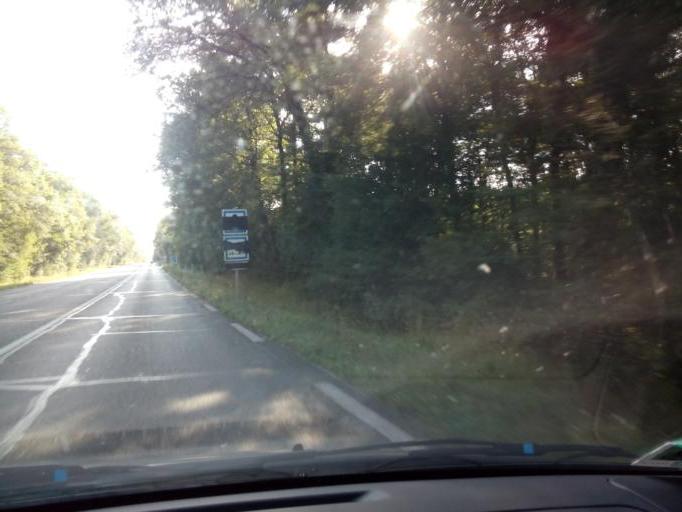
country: FR
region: Centre
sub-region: Departement d'Indre-et-Loire
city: Sache
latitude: 47.2902
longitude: 0.5277
